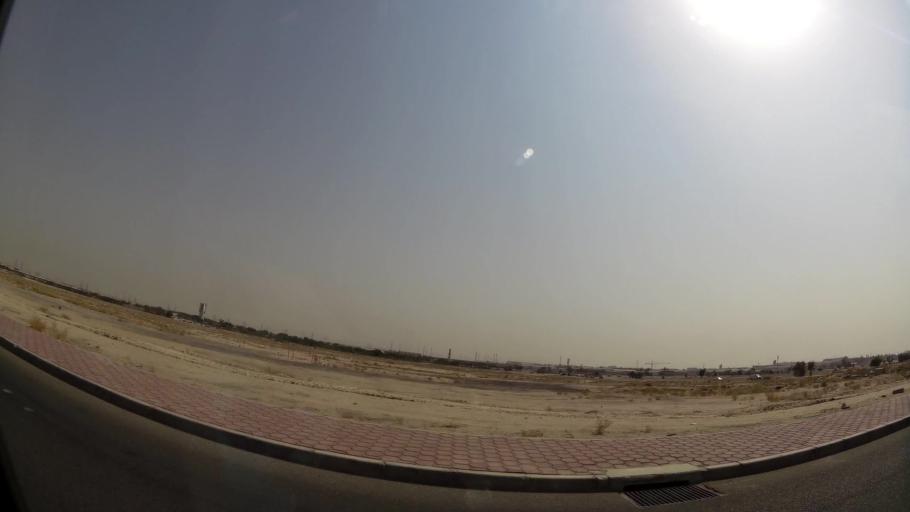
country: KW
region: Muhafazat al Jahra'
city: Al Jahra'
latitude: 29.3192
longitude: 47.7416
